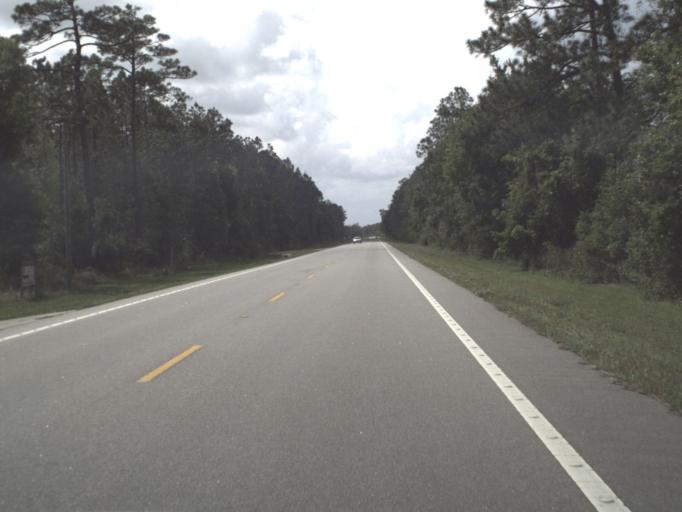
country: US
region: Florida
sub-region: Flagler County
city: Bunnell
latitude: 29.4760
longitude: -81.3326
